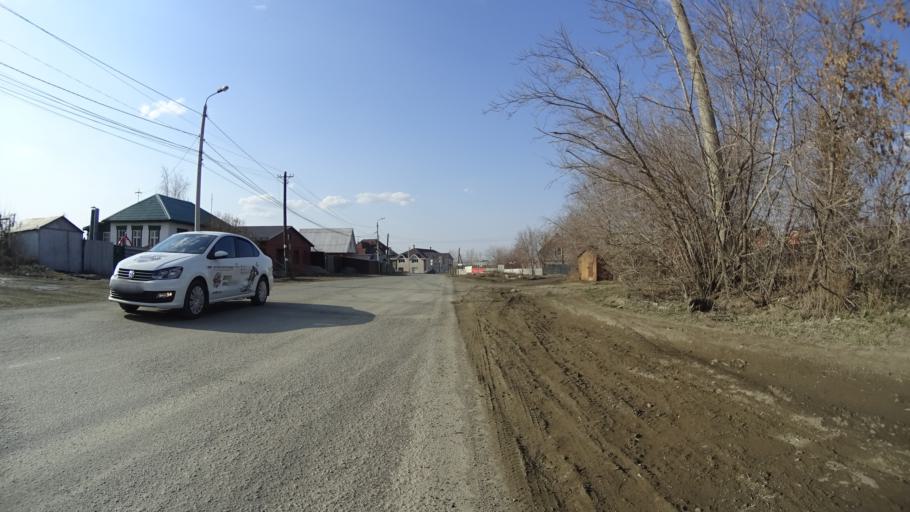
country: RU
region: Chelyabinsk
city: Novosineglazovskiy
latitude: 55.1099
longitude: 61.3331
